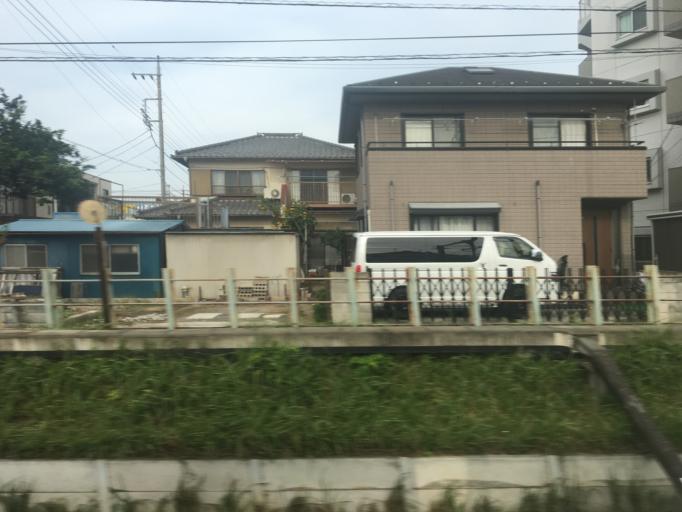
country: JP
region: Saitama
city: Kawagoe
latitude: 35.9020
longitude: 139.4703
